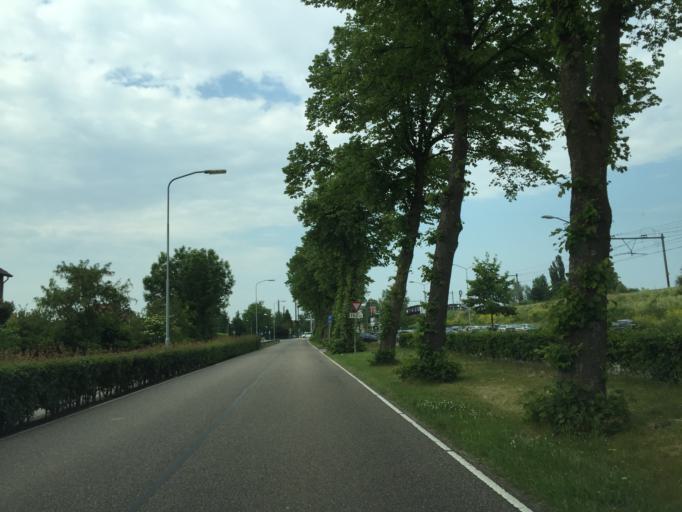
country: NL
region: Gelderland
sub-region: Gemeente Zaltbommel
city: Zaltbommel
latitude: 51.8056
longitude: 5.2631
